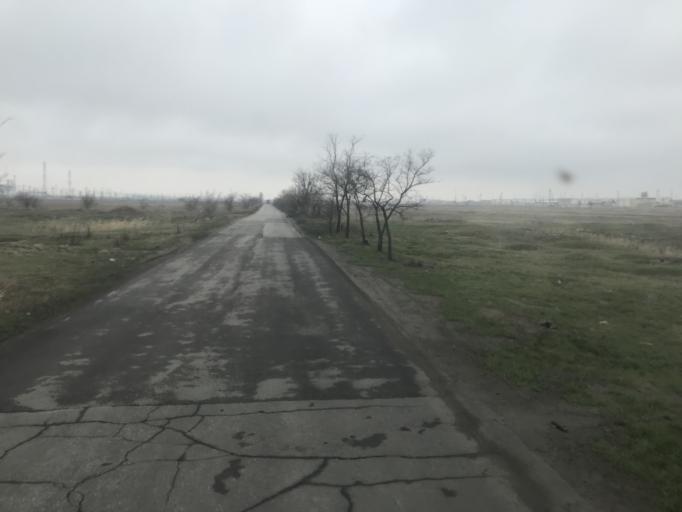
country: RU
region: Volgograd
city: Svetlyy Yar
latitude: 48.4983
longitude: 44.6488
